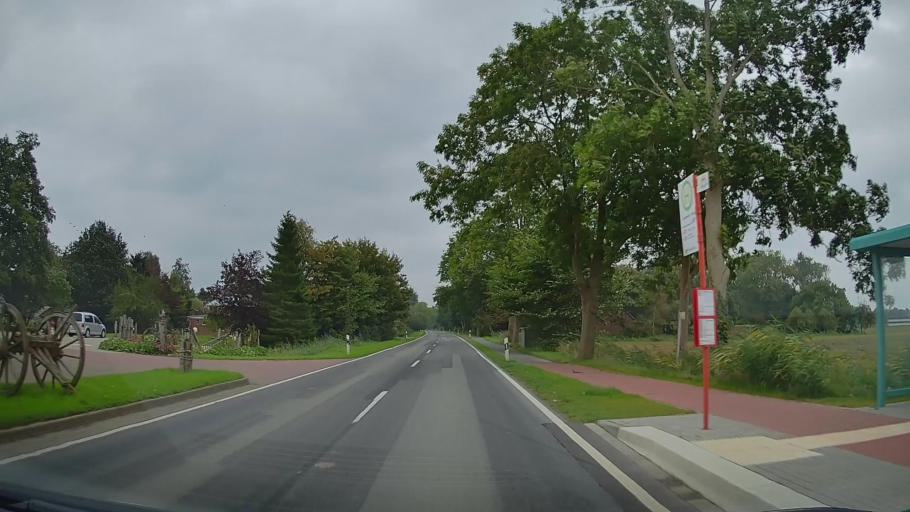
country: DE
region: Lower Saxony
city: Balje
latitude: 53.8116
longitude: 9.1202
